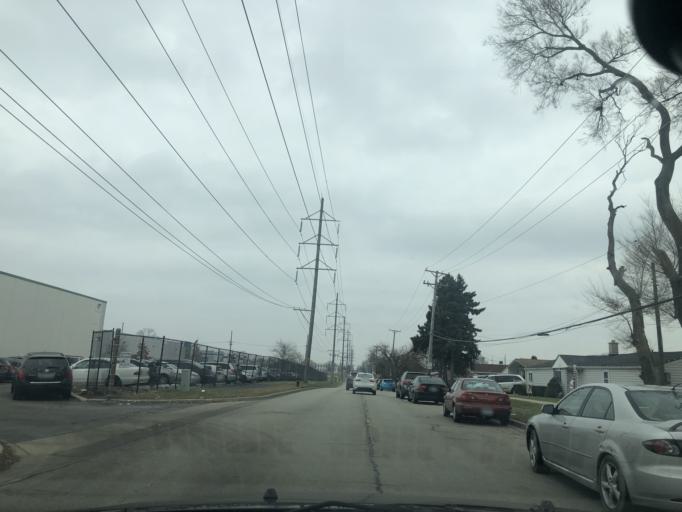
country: US
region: Illinois
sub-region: Cook County
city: Northlake
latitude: 41.9362
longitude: -87.8969
